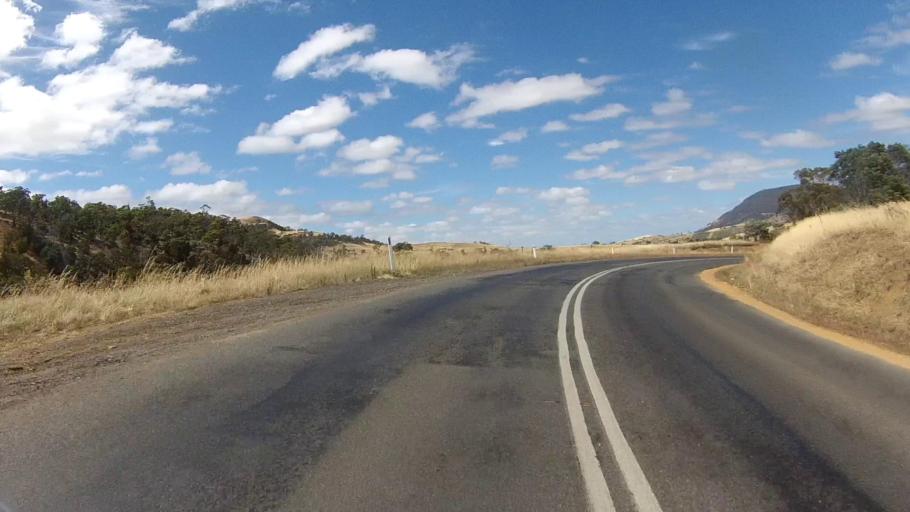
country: AU
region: Tasmania
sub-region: Brighton
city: Bridgewater
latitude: -42.5828
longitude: 147.4152
